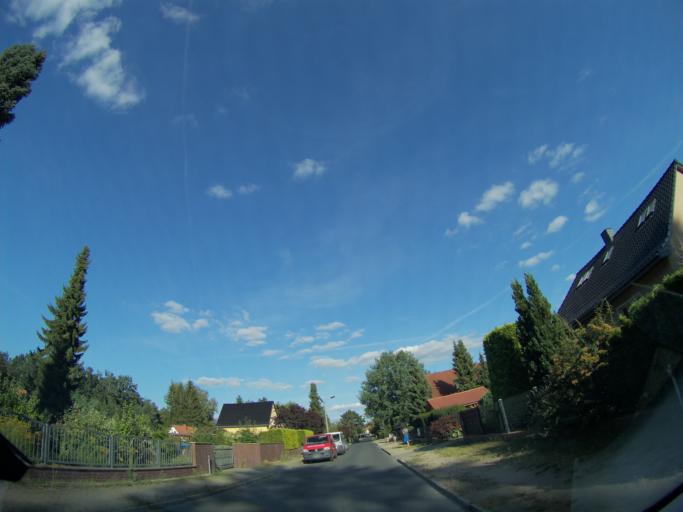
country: DE
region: Brandenburg
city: Stahnsdorf
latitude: 52.3813
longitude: 13.2001
